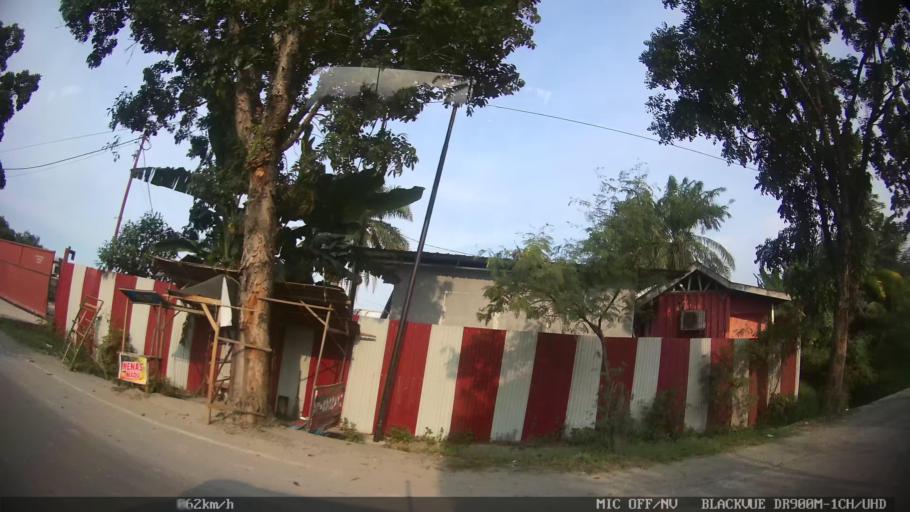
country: ID
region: North Sumatra
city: Binjai
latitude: 3.6120
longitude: 98.5344
